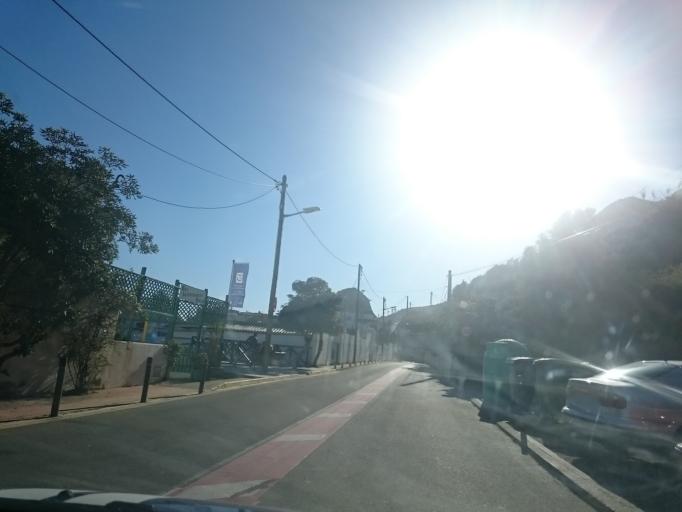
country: ES
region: Catalonia
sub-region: Provincia de Barcelona
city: Castelldefels
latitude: 41.2546
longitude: 1.9044
